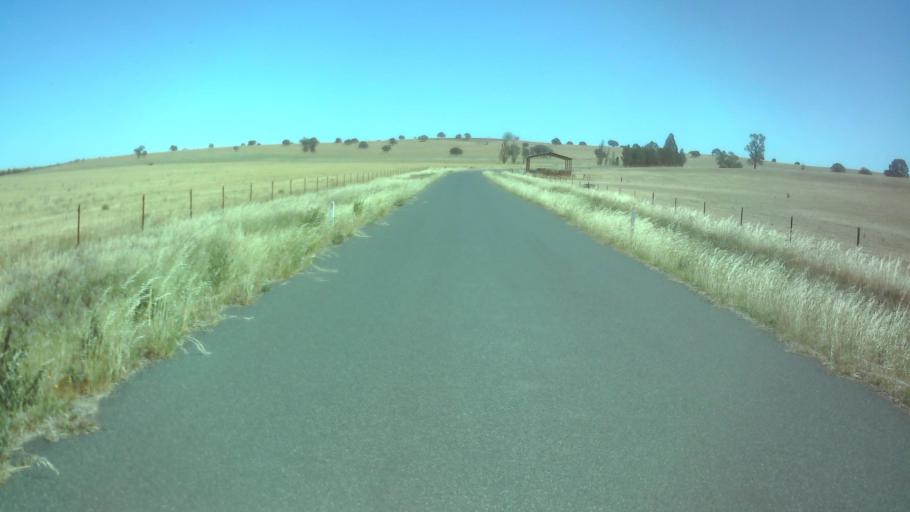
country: AU
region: New South Wales
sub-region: Weddin
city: Grenfell
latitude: -33.9814
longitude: 148.4034
